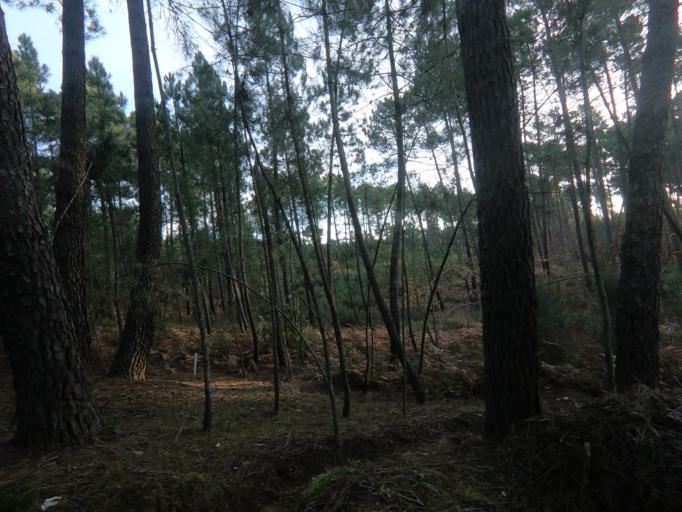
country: PT
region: Vila Real
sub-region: Sabrosa
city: Vilela
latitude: 41.2723
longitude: -7.6549
